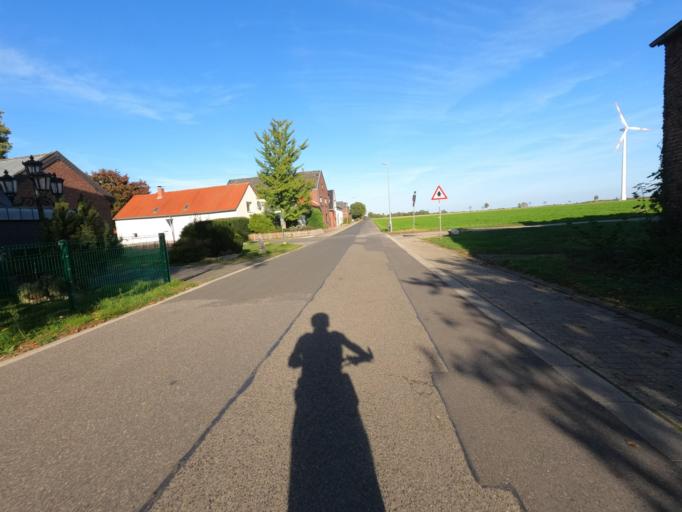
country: DE
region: North Rhine-Westphalia
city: Wegberg
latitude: 51.1284
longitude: 6.2235
